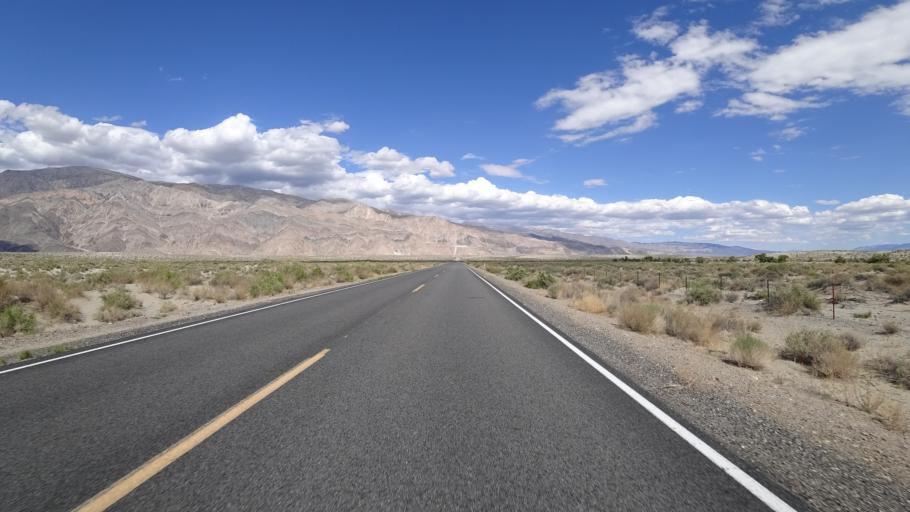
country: US
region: California
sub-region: Inyo County
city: Lone Pine
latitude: 36.5742
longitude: -118.0035
